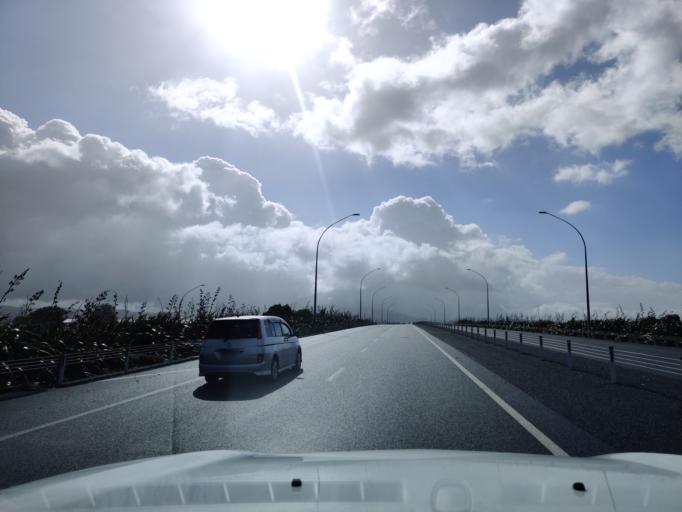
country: NZ
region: Waikato
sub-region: Waipa District
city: Cambridge
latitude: -37.8685
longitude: 175.4547
